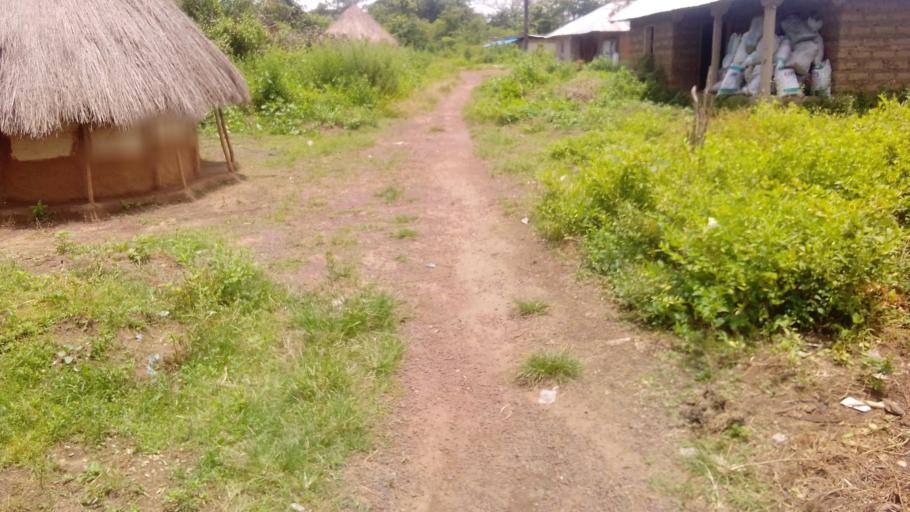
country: SL
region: Northern Province
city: Makeni
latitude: 9.0527
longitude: -12.1868
